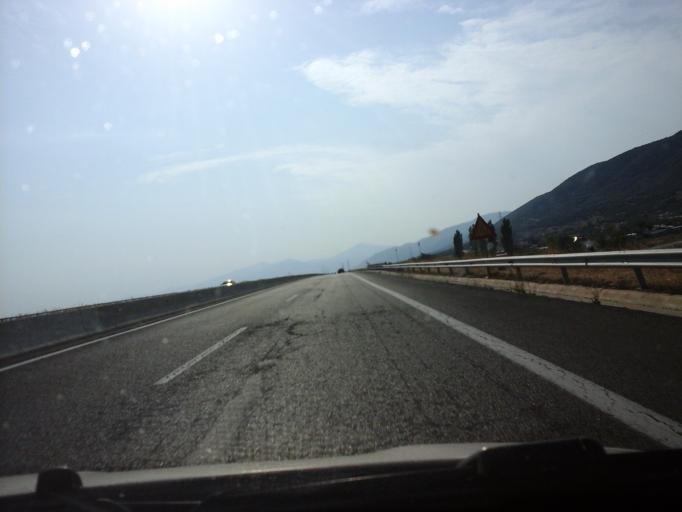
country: GR
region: East Macedonia and Thrace
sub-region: Nomos Rodopis
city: Iasmos
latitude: 41.1138
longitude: 25.1267
